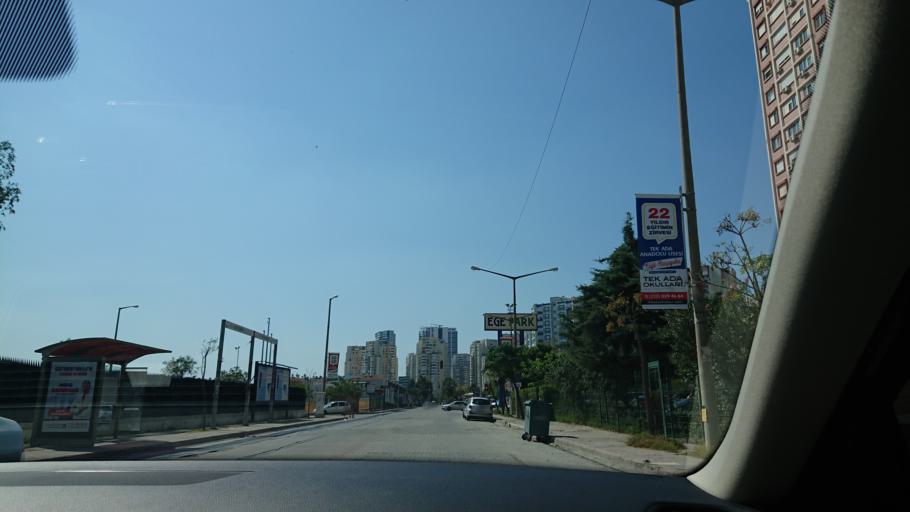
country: TR
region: Izmir
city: Karsiyaka
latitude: 38.4698
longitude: 27.0764
